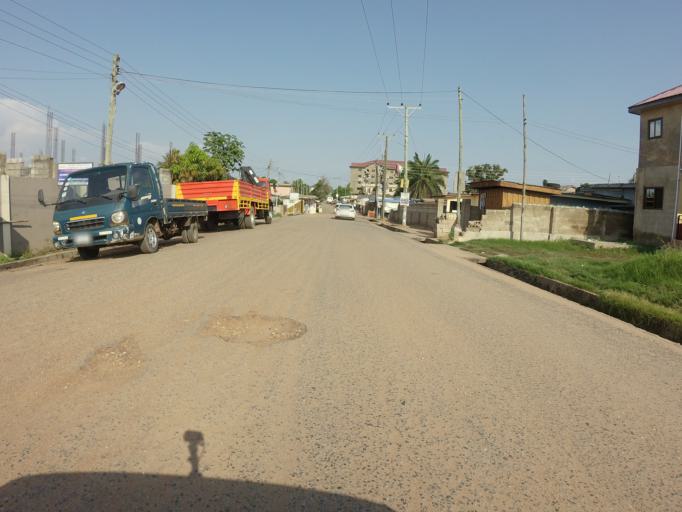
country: GH
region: Greater Accra
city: Dome
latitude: 5.6130
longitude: -0.2395
